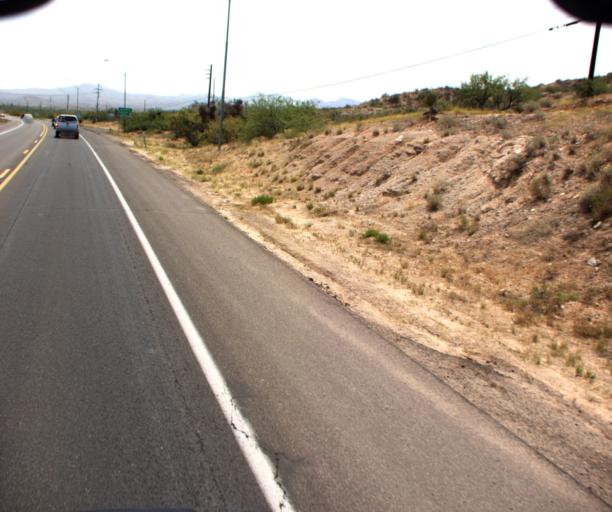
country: US
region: Arizona
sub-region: Gila County
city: Globe
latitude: 33.3748
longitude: -110.7416
